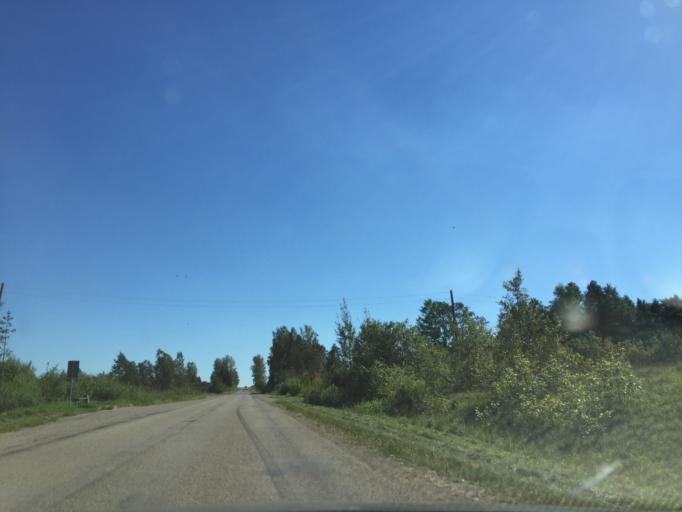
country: LV
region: Akniste
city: Akniste
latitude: 56.0348
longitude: 25.9106
